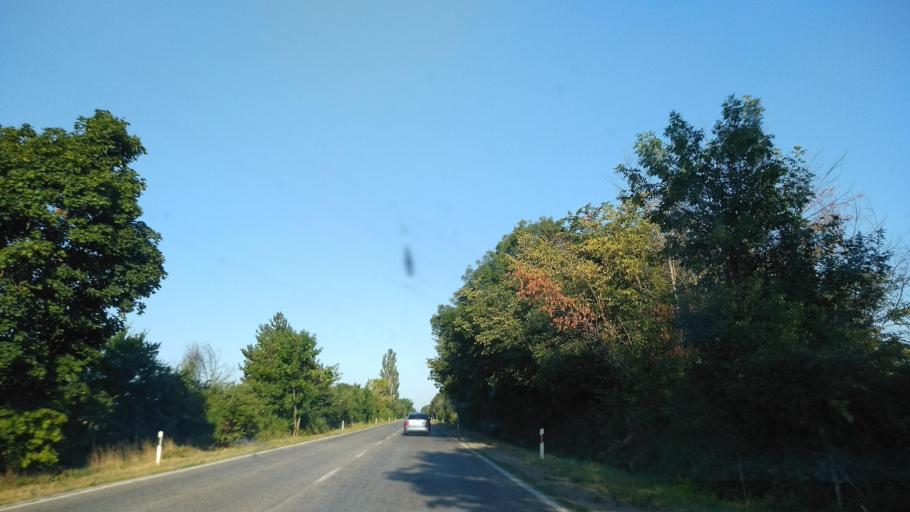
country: BG
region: Gabrovo
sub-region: Obshtina Dryanovo
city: Dryanovo
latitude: 43.0878
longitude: 25.4572
